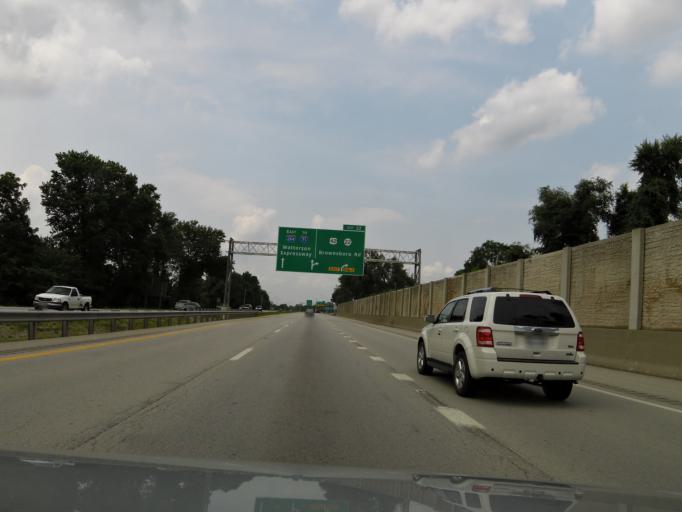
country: US
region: Kentucky
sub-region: Jefferson County
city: Windy Hills
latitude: 38.2734
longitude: -85.6298
